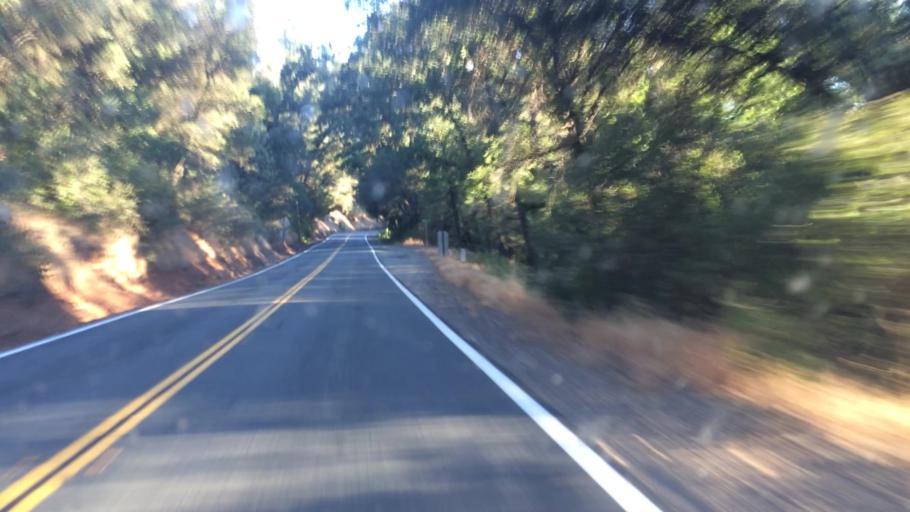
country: US
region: California
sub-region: Amador County
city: Plymouth
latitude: 38.5410
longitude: -120.8477
